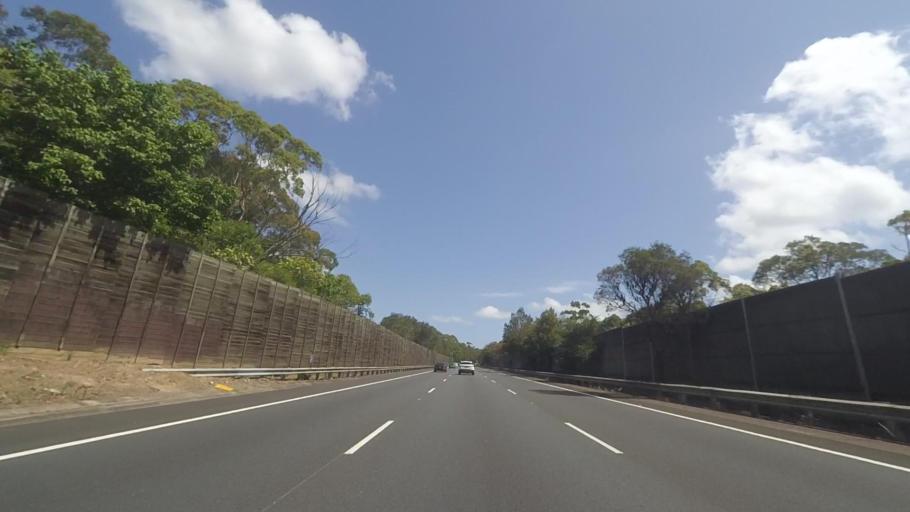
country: AU
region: New South Wales
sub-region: Ku-ring-gai
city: North Wahroonga
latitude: -33.7014
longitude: 151.1182
